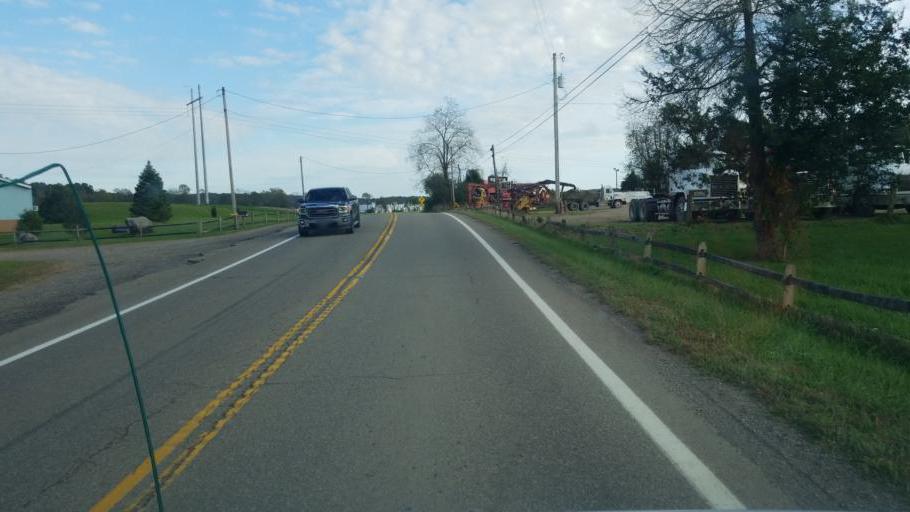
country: US
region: Ohio
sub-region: Holmes County
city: Millersburg
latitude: 40.6439
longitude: -81.9346
